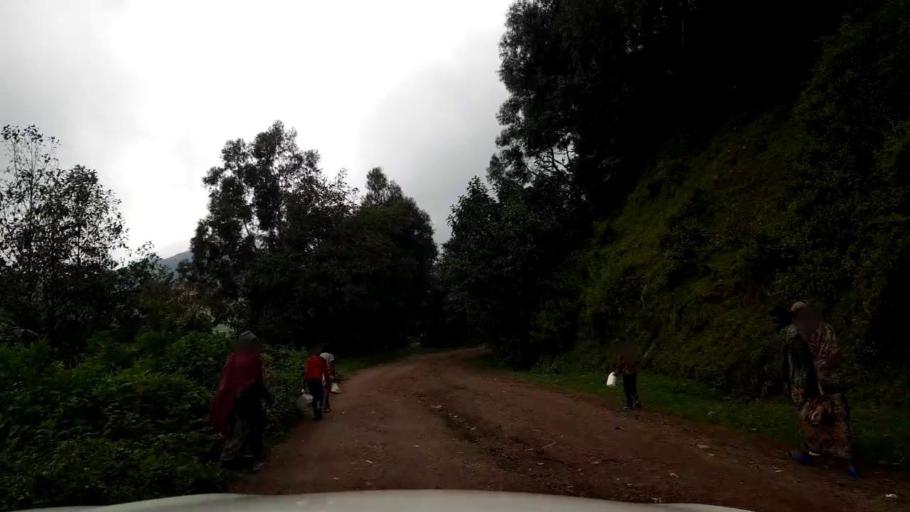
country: RW
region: Western Province
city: Gisenyi
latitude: -1.6570
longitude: 29.4184
